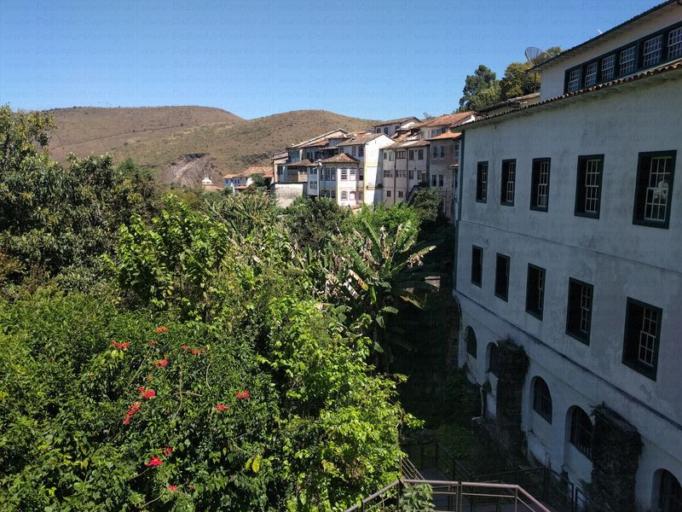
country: BR
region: Minas Gerais
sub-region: Ouro Preto
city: Ouro Preto
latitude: -20.3844
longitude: -43.5064
